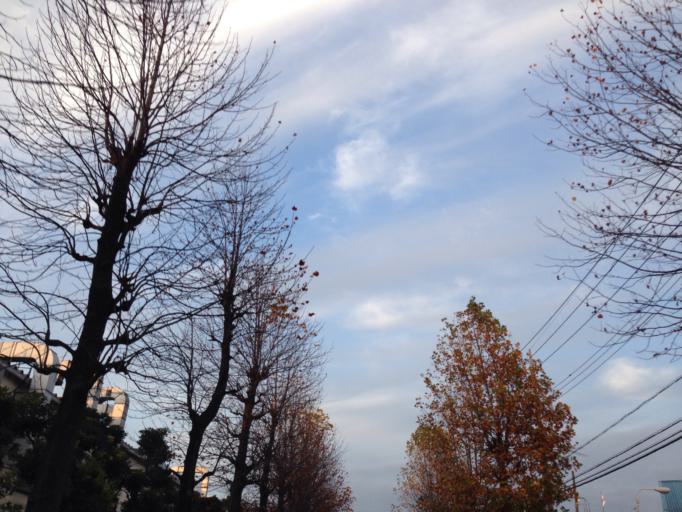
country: JP
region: Chiba
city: Kashiwa
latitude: 35.9046
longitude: 139.9441
